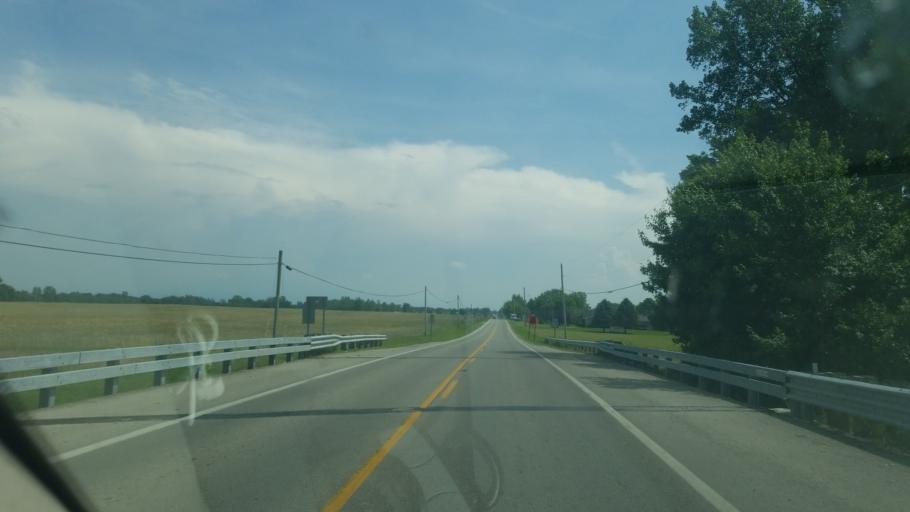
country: US
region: Ohio
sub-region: Logan County
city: Northwood
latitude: 40.5037
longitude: -83.7436
